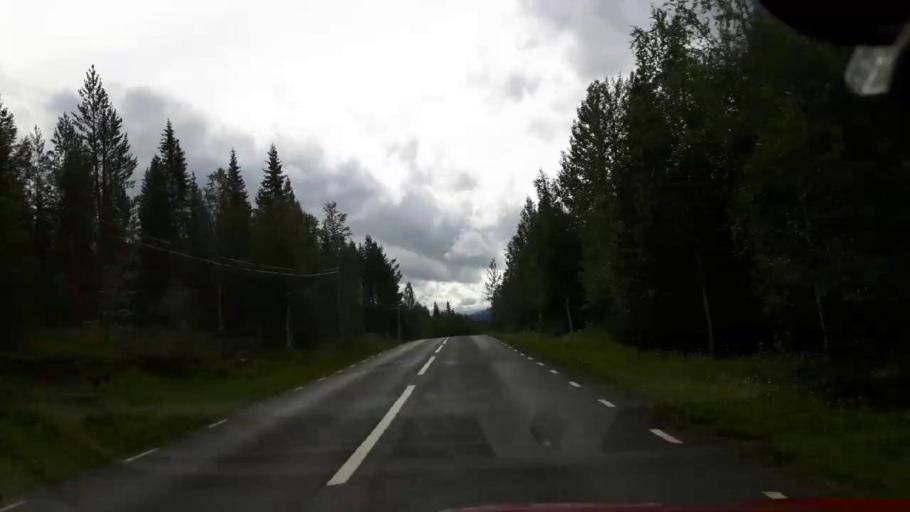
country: NO
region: Nord-Trondelag
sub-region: Lierne
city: Sandvika
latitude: 64.5199
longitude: 14.1628
